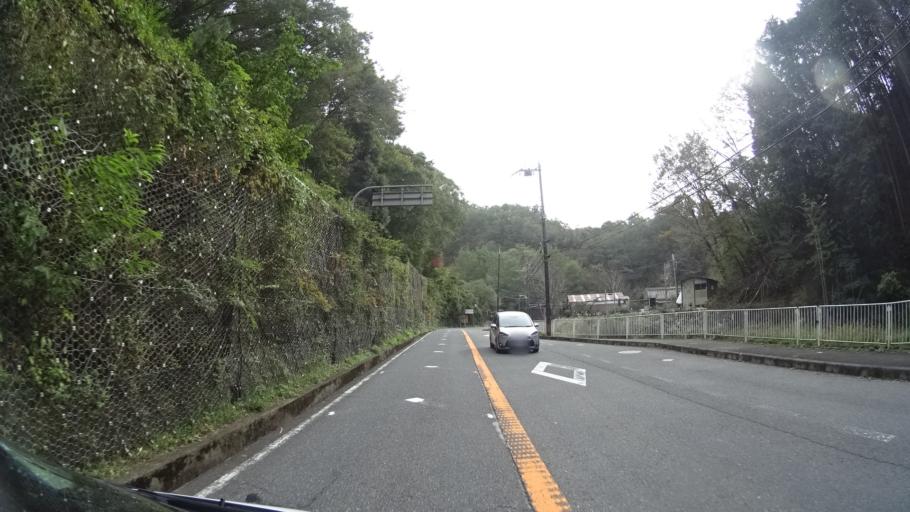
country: JP
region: Shiga Prefecture
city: Otsu-shi
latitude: 35.0402
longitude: 135.8263
